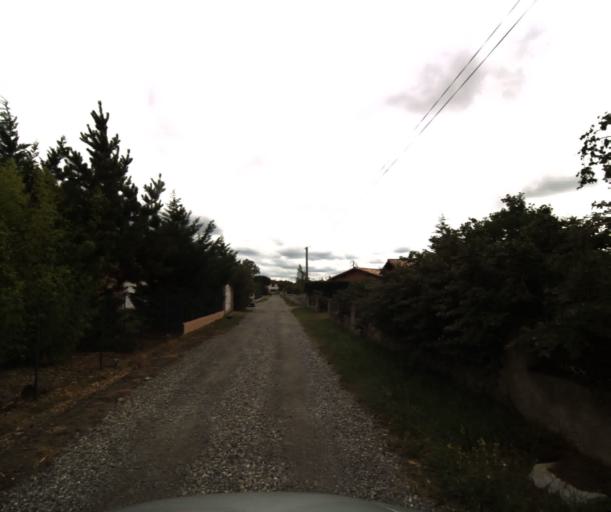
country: FR
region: Midi-Pyrenees
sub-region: Departement de la Haute-Garonne
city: Muret
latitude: 43.4576
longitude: 1.3574
